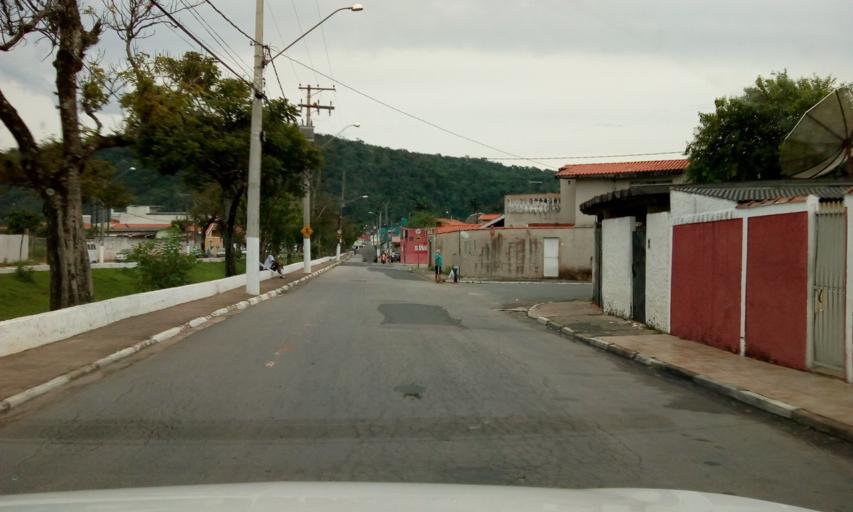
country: BR
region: Sao Paulo
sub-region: Itupeva
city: Itupeva
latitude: -23.1541
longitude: -47.0534
